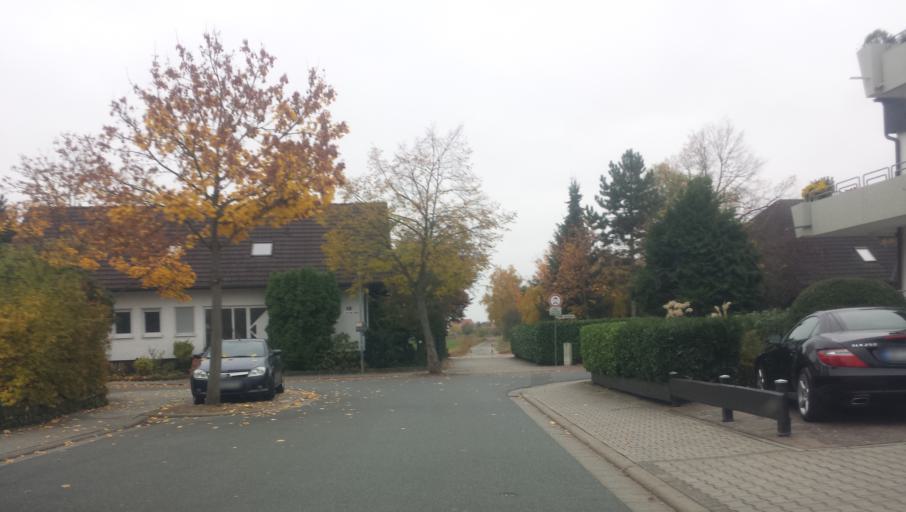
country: DE
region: Hesse
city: Zwingenberg
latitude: 49.7379
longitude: 8.6138
